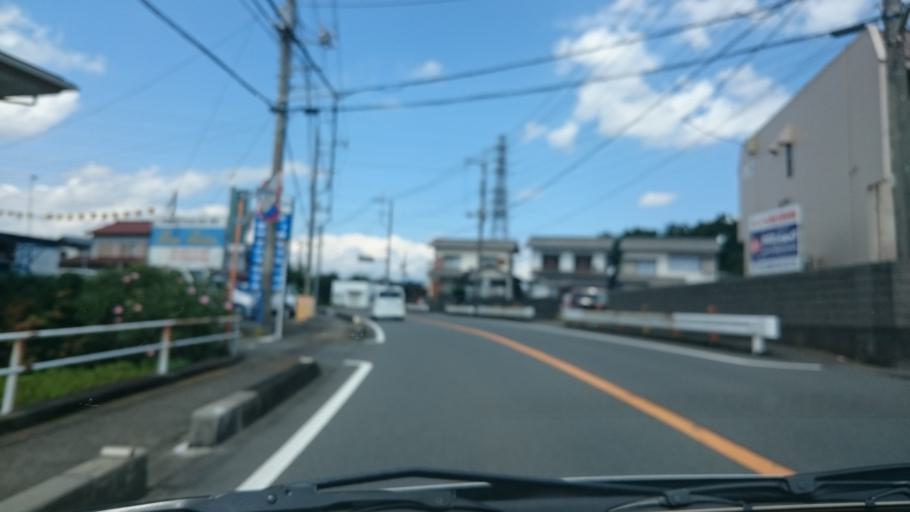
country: JP
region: Shizuoka
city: Gotemba
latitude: 35.2197
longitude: 138.9211
